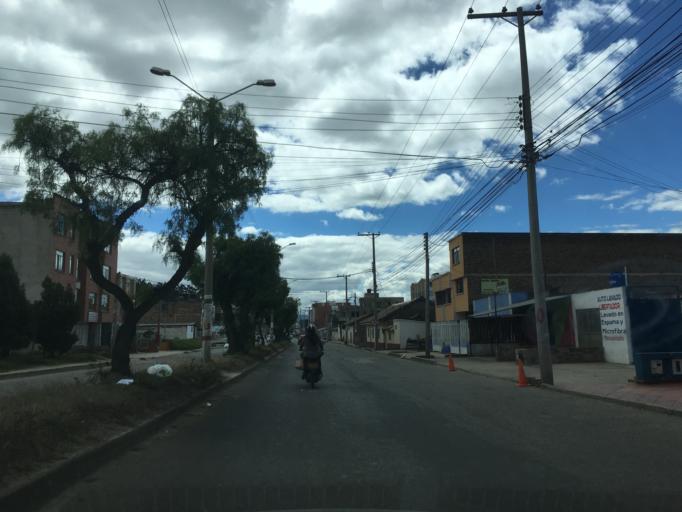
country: CO
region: Boyaca
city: Sogamoso
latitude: 5.7071
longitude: -72.9347
